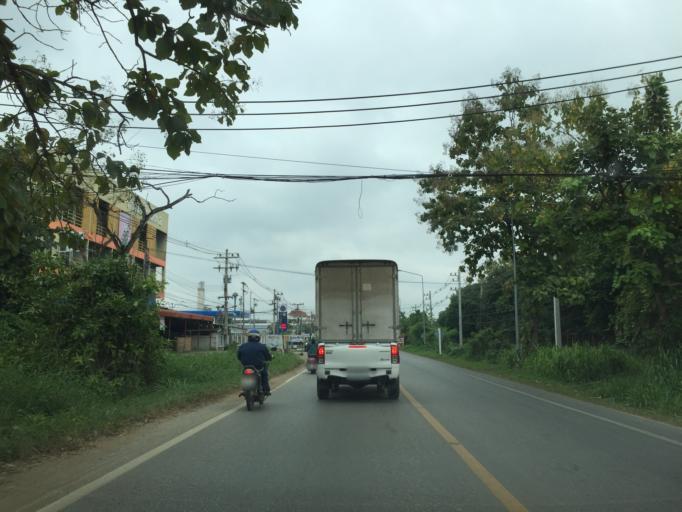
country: TH
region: Lamphun
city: Lamphun
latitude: 18.5832
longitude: 99.0576
